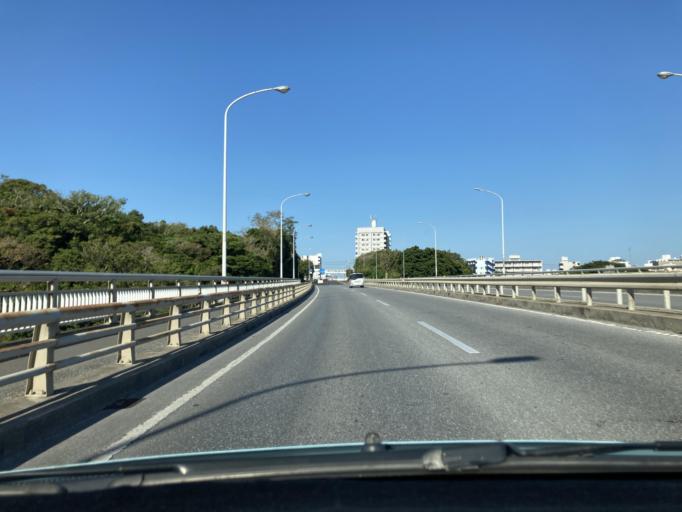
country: JP
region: Okinawa
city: Ginowan
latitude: 26.2519
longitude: 127.7510
